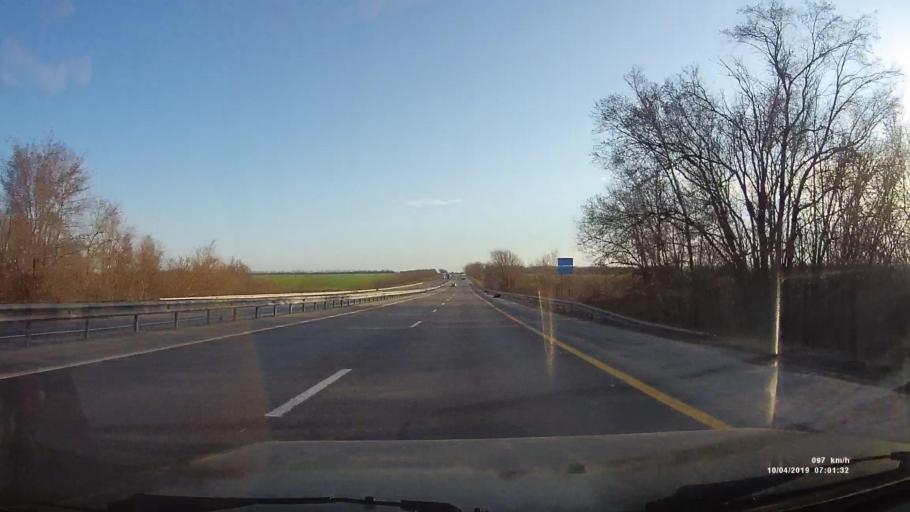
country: RU
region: Rostov
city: Krasyukovskaya
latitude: 47.5965
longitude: 39.9844
